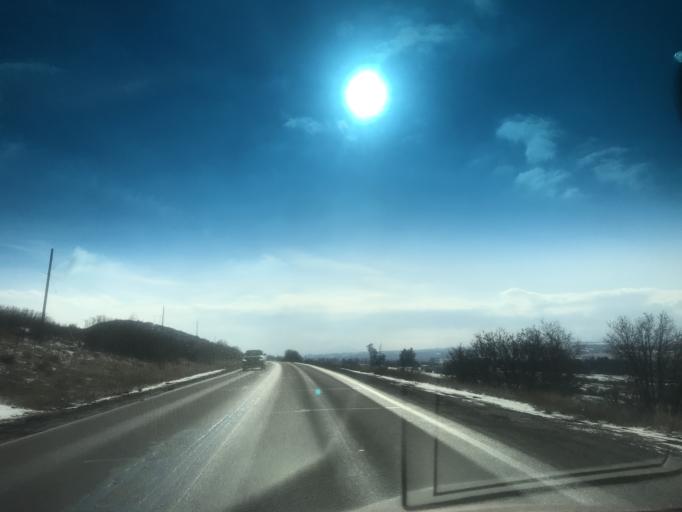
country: US
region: Colorado
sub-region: Douglas County
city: Castle Pines
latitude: 39.4644
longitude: -104.9868
